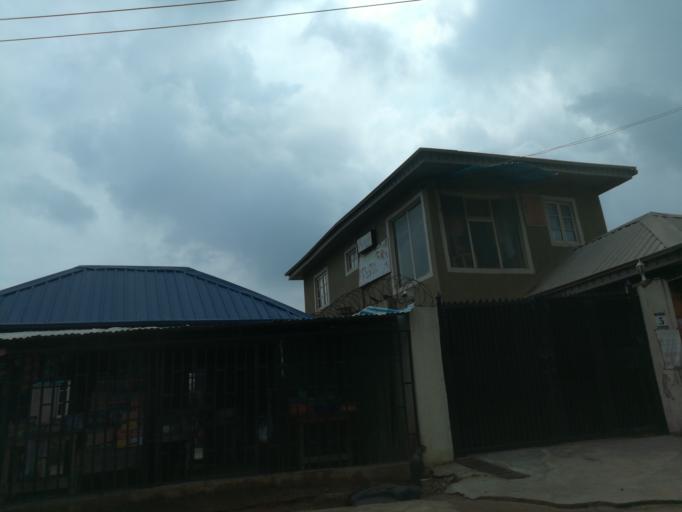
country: NG
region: Lagos
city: Oshodi
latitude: 6.5823
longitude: 3.3070
